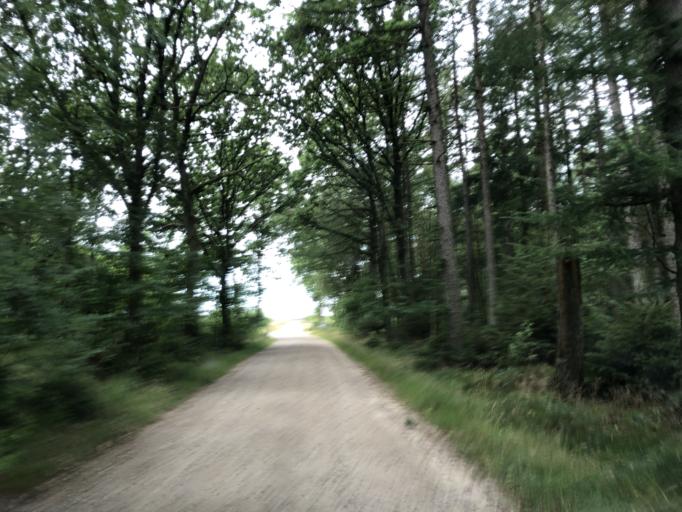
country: DK
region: Central Jutland
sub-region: Holstebro Kommune
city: Holstebro
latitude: 56.2445
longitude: 8.5006
